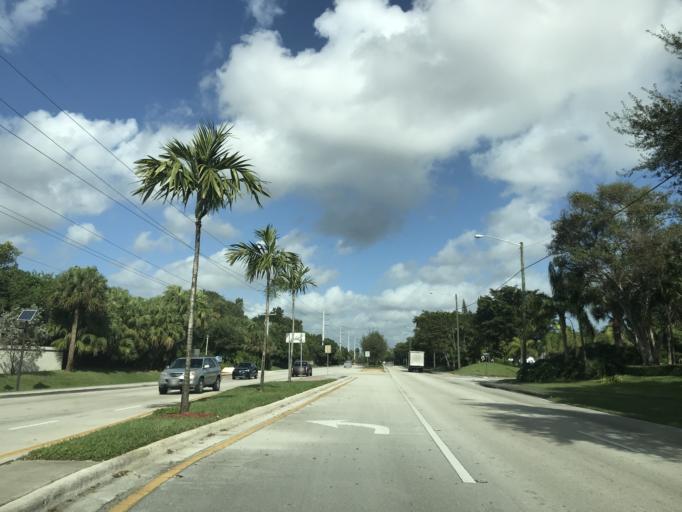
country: US
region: Florida
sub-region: Broward County
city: Coconut Creek
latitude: 26.2609
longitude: -80.1863
